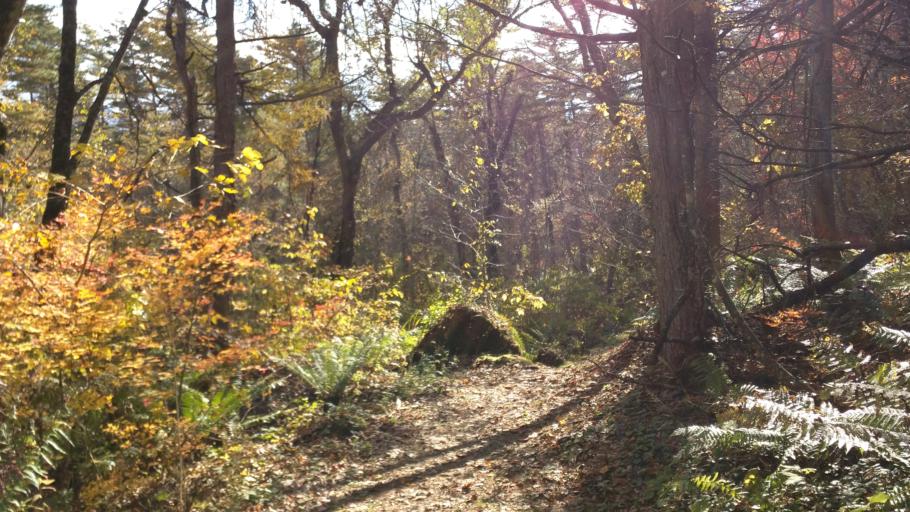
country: JP
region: Fukushima
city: Inawashiro
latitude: 37.6534
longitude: 140.0717
